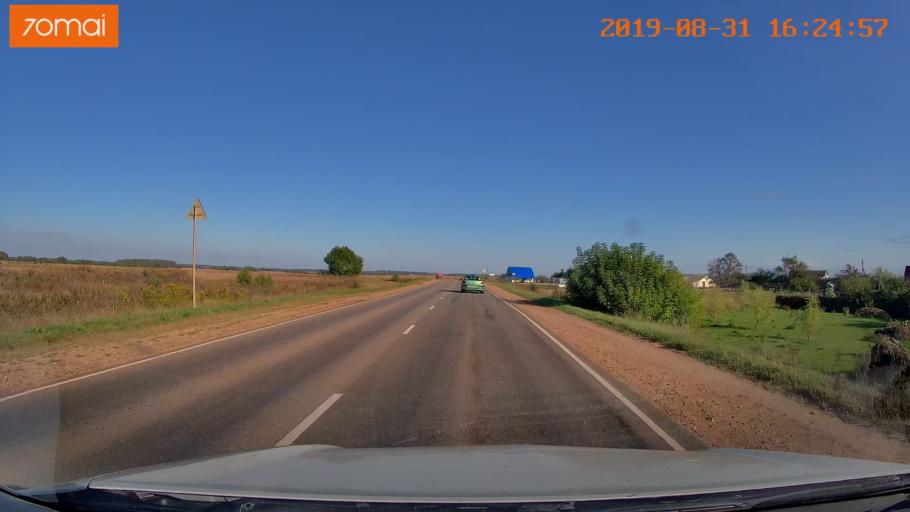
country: RU
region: Kaluga
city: Babynino
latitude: 54.5200
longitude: 35.7036
